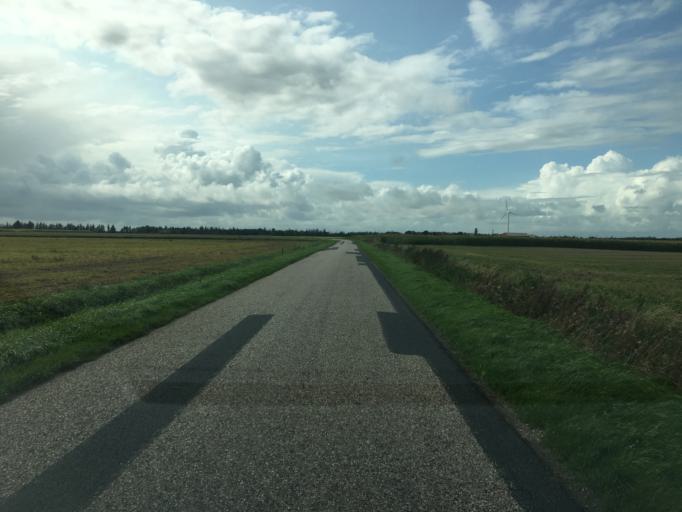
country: DK
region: South Denmark
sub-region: Tonder Kommune
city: Tonder
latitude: 54.9782
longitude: 8.8529
